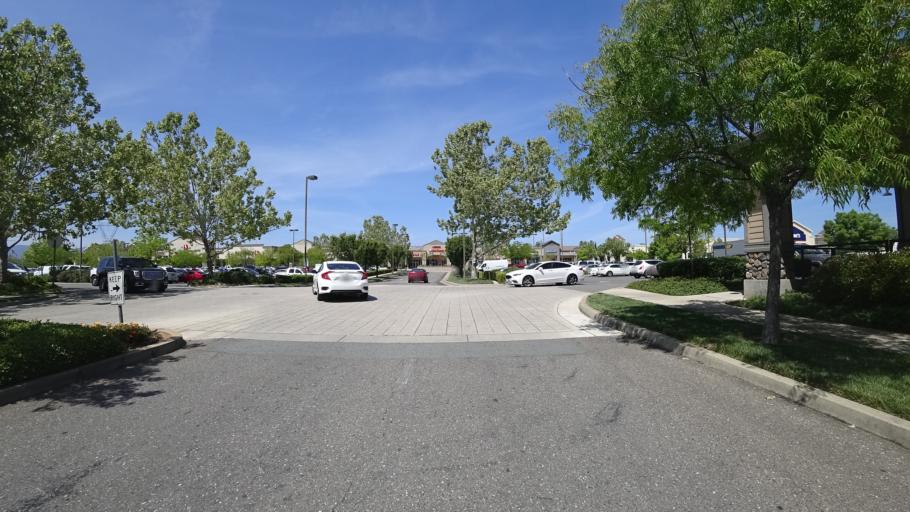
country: US
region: California
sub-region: Shasta County
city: Redding
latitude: 40.5714
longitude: -122.3504
